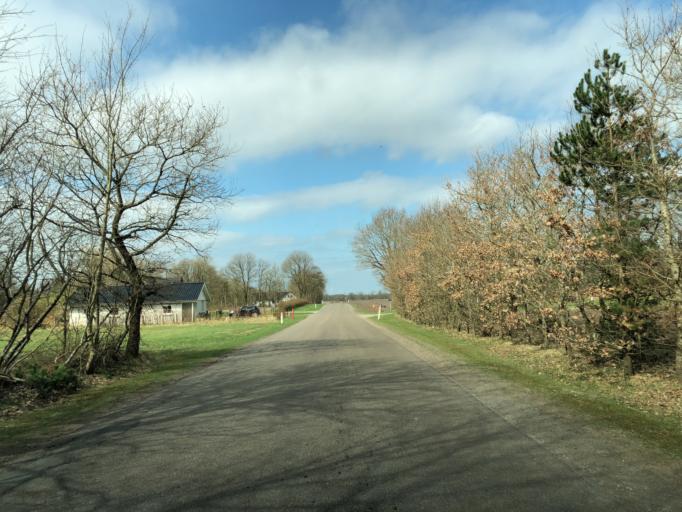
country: DK
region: South Denmark
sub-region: Vejle Kommune
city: Give
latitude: 55.9124
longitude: 9.2491
